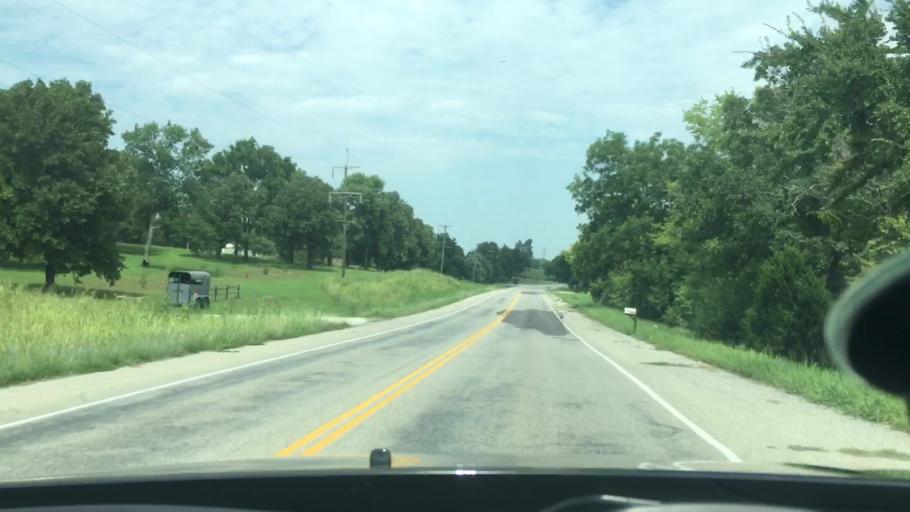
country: US
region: Oklahoma
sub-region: Pontotoc County
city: Byng
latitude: 34.8314
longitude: -96.6787
